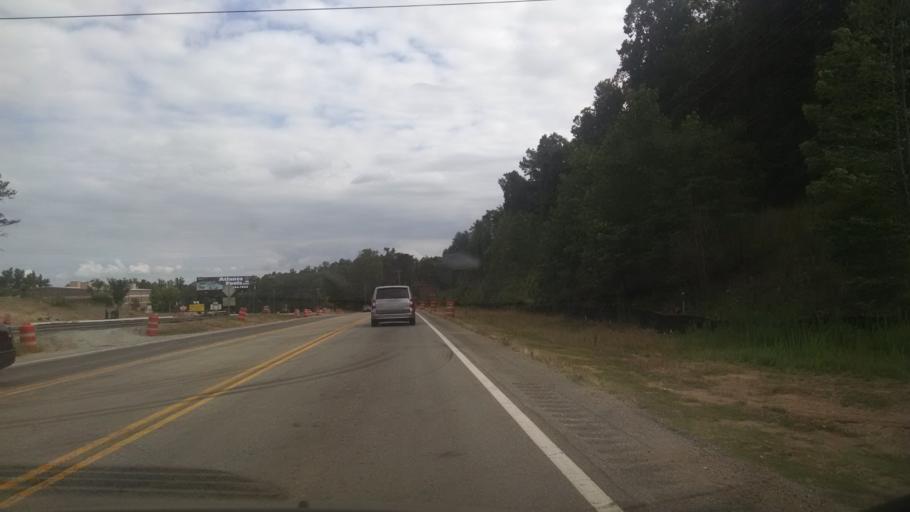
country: US
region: Georgia
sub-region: Forsyth County
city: Cumming
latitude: 34.1442
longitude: -84.1050
